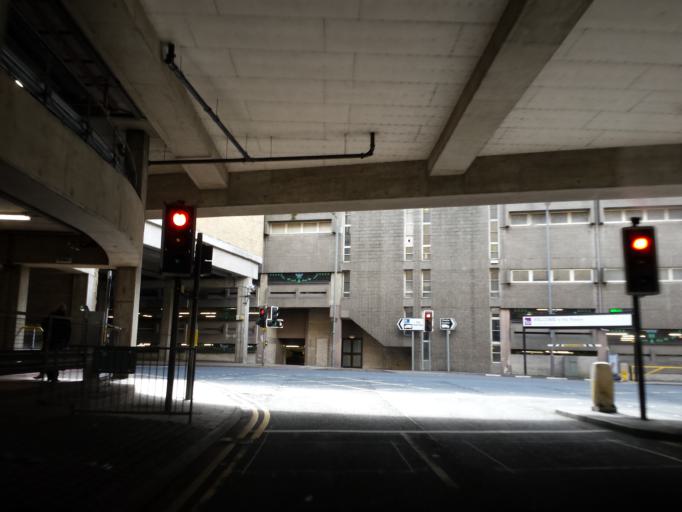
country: GB
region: Scotland
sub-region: Stirling
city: Stirling
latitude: 56.1175
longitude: -3.9339
